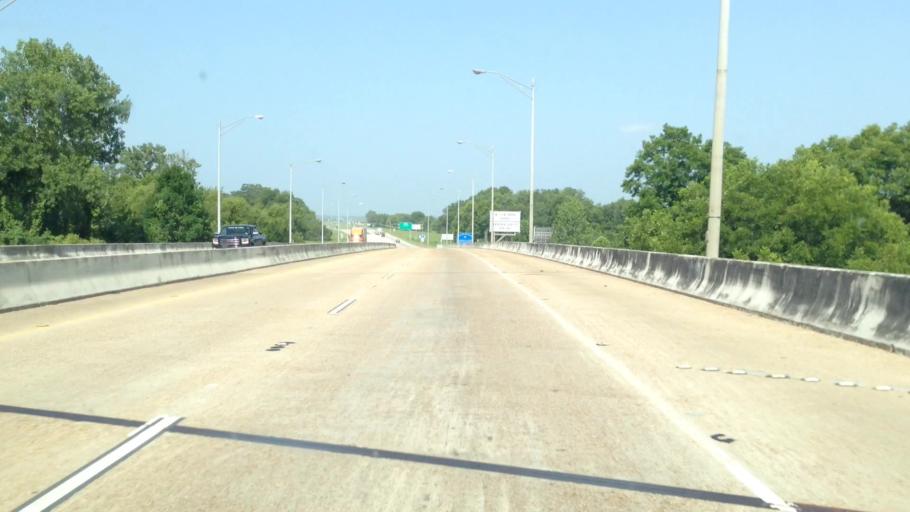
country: US
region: Mississippi
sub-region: Warren County
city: Vicksburg
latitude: 32.3217
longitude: -90.9306
